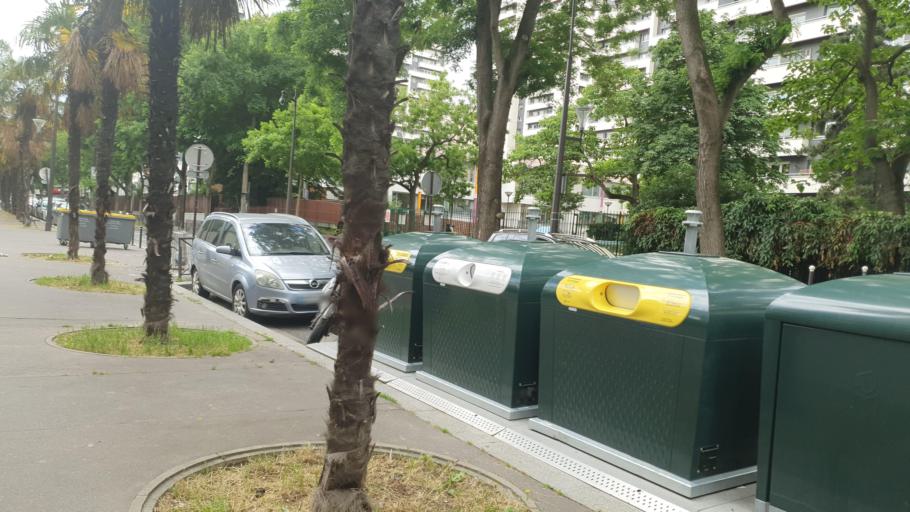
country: FR
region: Ile-de-France
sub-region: Departement de Seine-Saint-Denis
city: Aubervilliers
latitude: 48.8957
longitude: 2.3755
